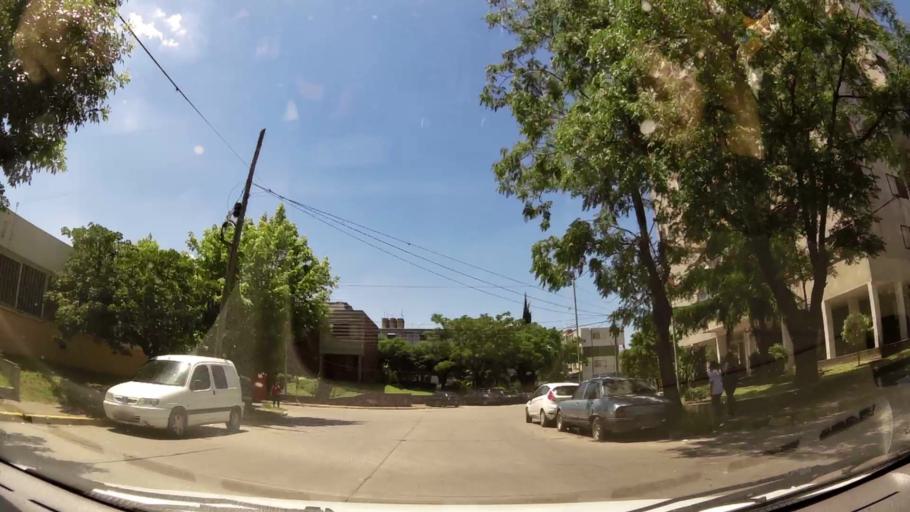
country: AR
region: Buenos Aires
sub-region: Partido de Merlo
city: Merlo
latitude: -34.6525
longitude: -58.7101
